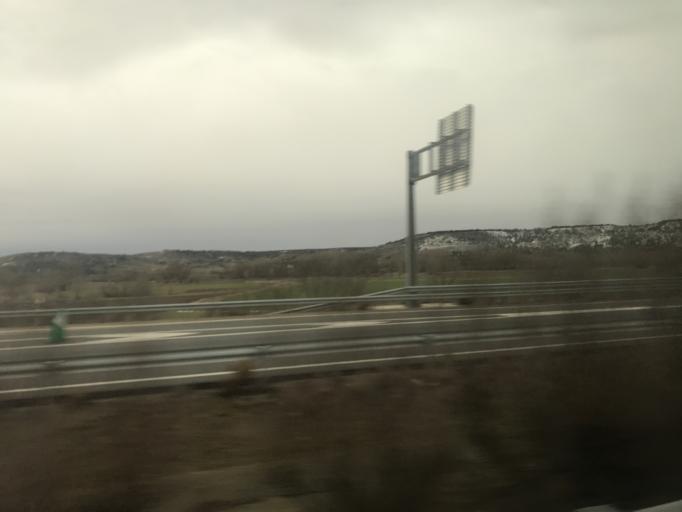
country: ES
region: Castille and Leon
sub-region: Provincia de Burgos
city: Celada del Camino
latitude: 42.2596
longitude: -3.9436
